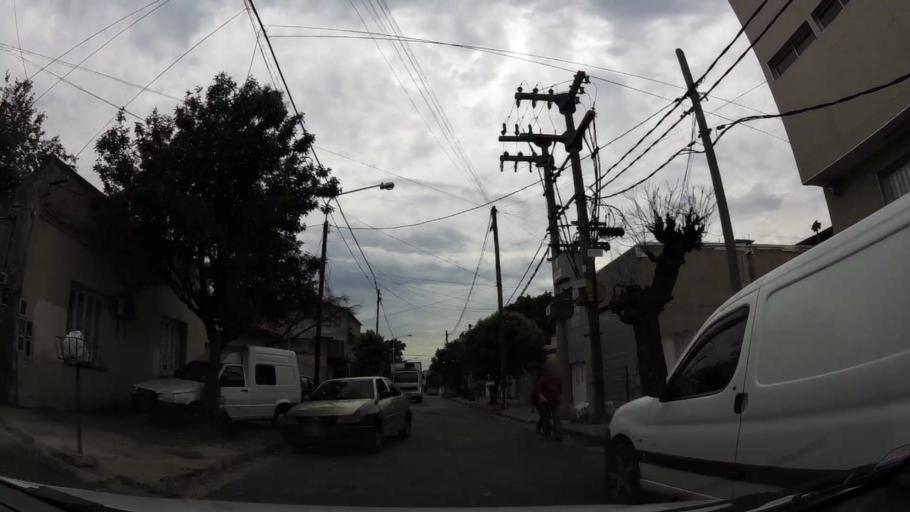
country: AR
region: Buenos Aires F.D.
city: Villa Lugano
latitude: -34.6816
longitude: -58.5066
